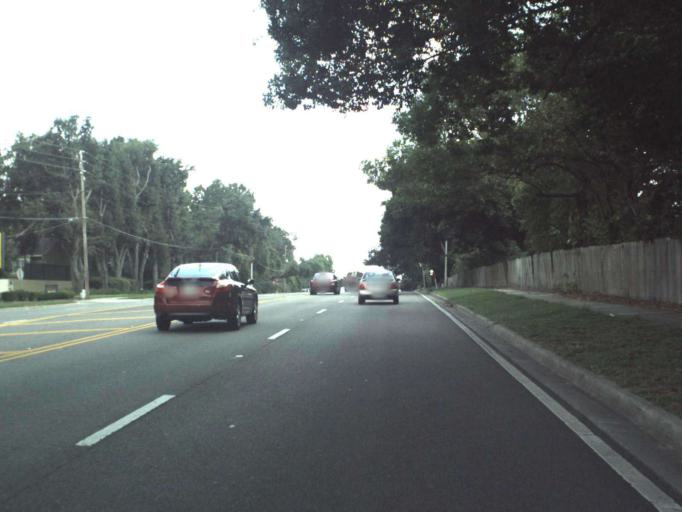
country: US
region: Florida
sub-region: Seminole County
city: Forest City
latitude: 28.6695
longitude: -81.4190
